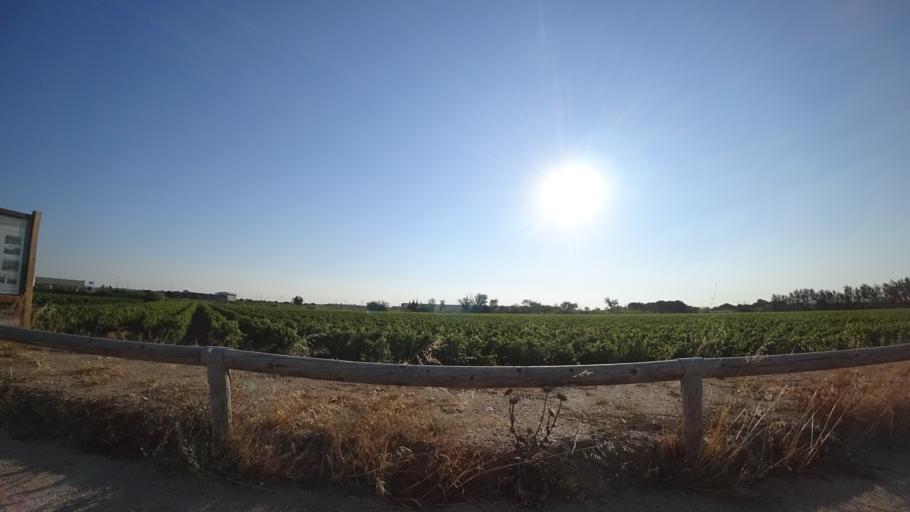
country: FR
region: Languedoc-Roussillon
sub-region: Departement des Pyrenees-Orientales
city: Pia
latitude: 42.7696
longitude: 2.9106
